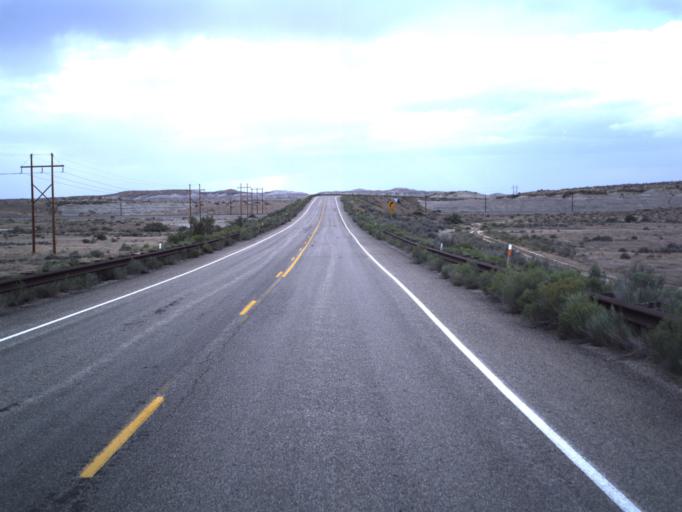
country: US
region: Colorado
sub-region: Rio Blanco County
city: Rangely
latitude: 40.0917
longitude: -109.2237
